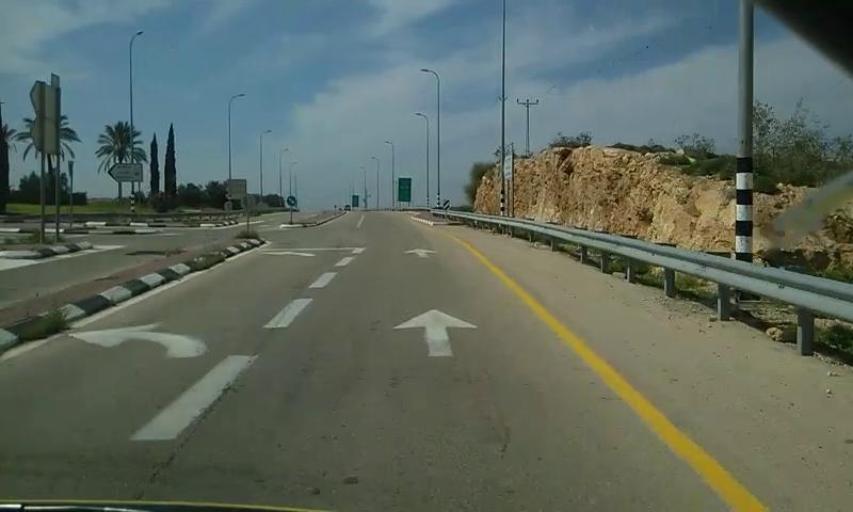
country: PS
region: West Bank
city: Az Zahiriyah
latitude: 31.3758
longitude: 35.0073
